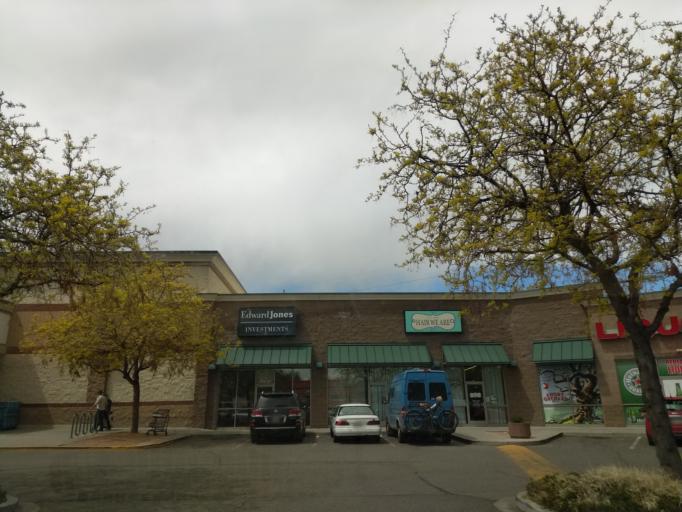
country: US
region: Colorado
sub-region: Mesa County
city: Grand Junction
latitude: 39.0667
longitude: -108.5879
